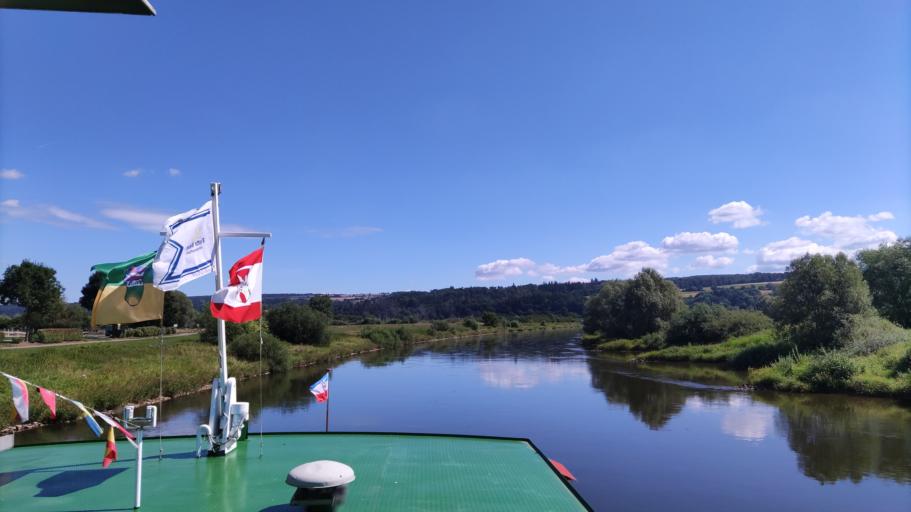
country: DE
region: North Rhine-Westphalia
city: Beverungen
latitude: 51.6691
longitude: 9.3829
